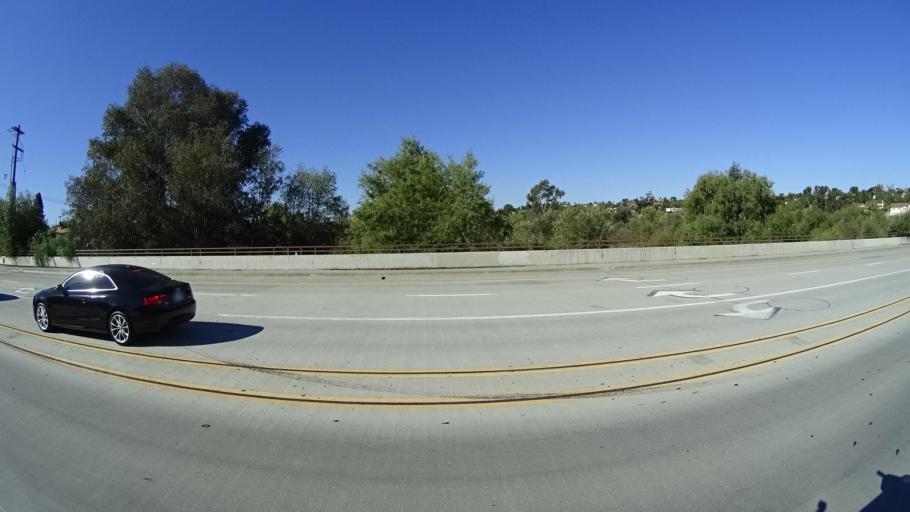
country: US
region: California
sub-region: San Diego County
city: Bonita
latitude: 32.6750
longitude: -117.0163
